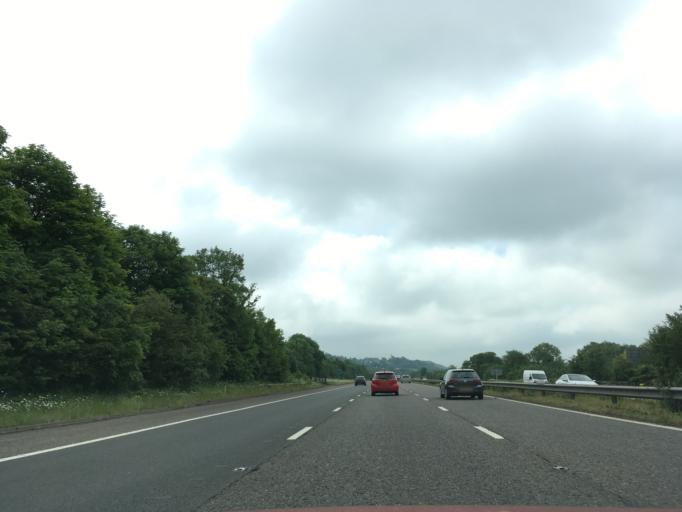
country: GB
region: England
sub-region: Devon
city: Cullompton
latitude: 50.8608
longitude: -3.3836
